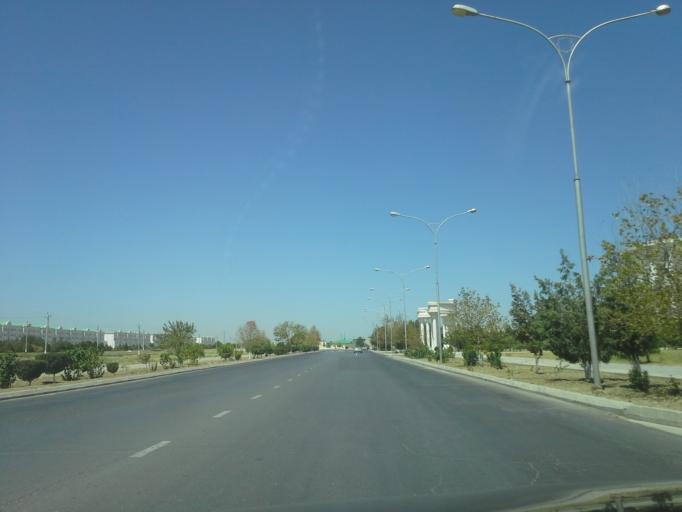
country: TM
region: Ahal
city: Ashgabat
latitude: 37.9902
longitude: 58.3238
